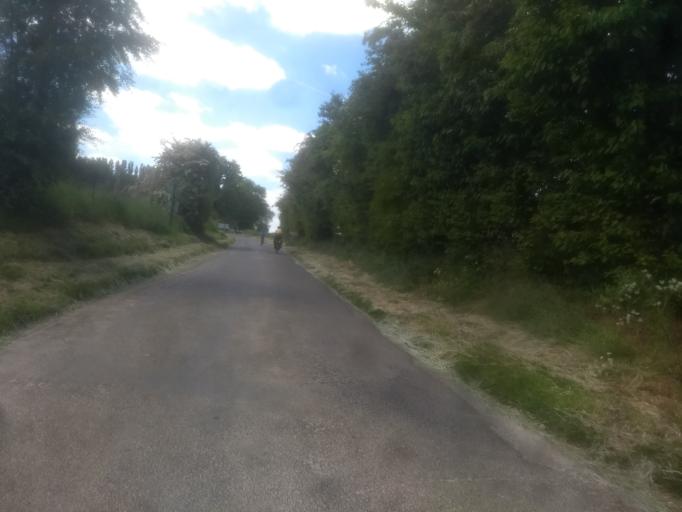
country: FR
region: Nord-Pas-de-Calais
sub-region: Departement du Pas-de-Calais
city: Beaumetz-les-Loges
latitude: 50.2287
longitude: 2.6737
